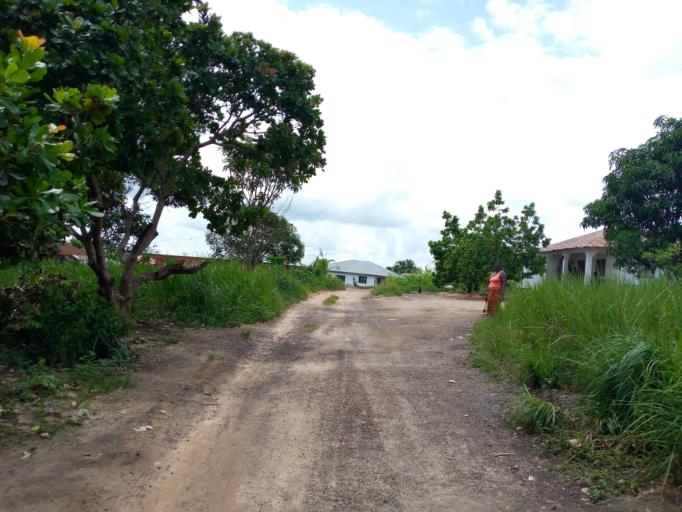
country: SL
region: Northern Province
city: Magburaka
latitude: 8.7297
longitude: -11.9398
